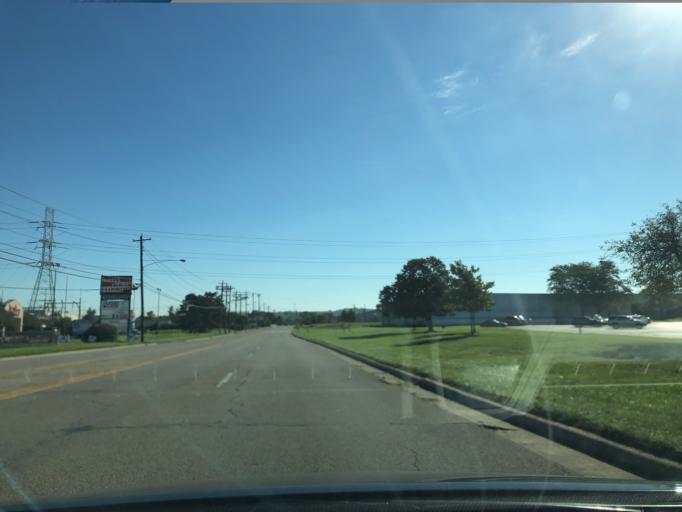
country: US
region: Ohio
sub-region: Hamilton County
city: Glendale
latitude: 39.2848
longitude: -84.4378
